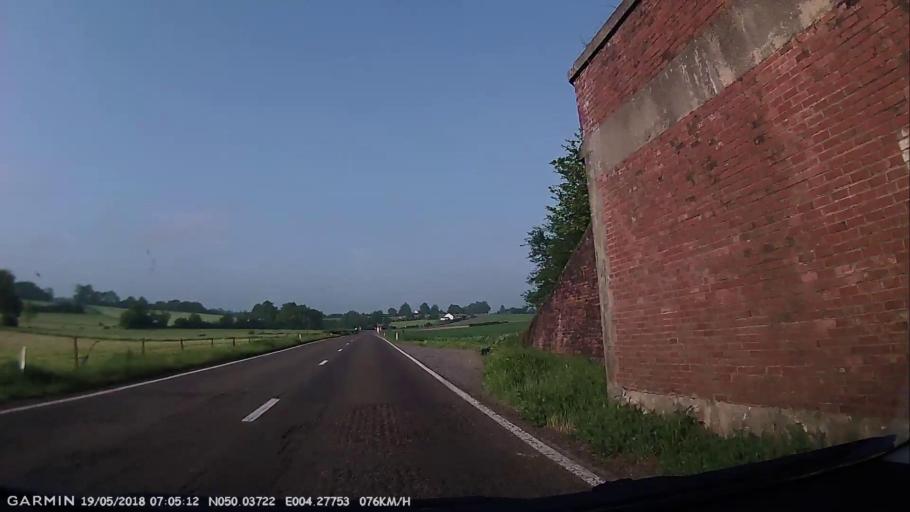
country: BE
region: Wallonia
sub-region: Province du Hainaut
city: Chimay
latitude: 50.0371
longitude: 4.2774
